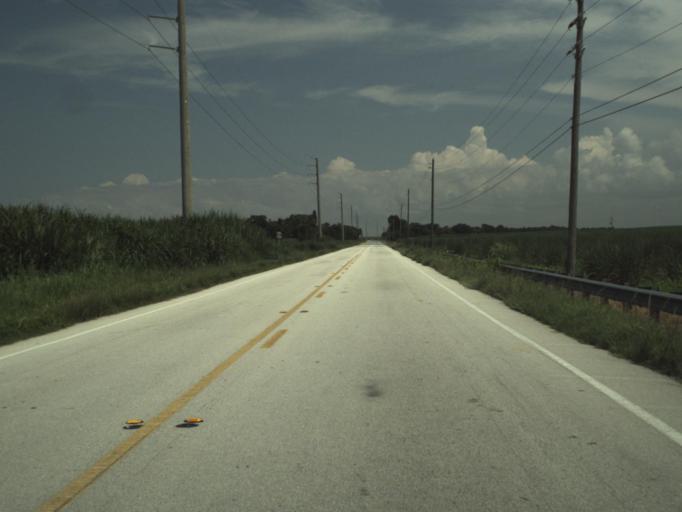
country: US
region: Florida
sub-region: Palm Beach County
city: Pahokee
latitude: 26.9086
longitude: -80.6120
